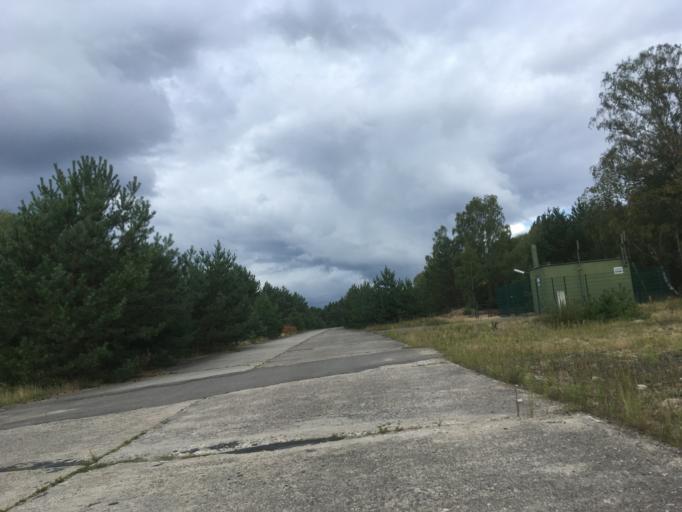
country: DE
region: Brandenburg
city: Halbe
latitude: 52.0428
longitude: 13.7500
